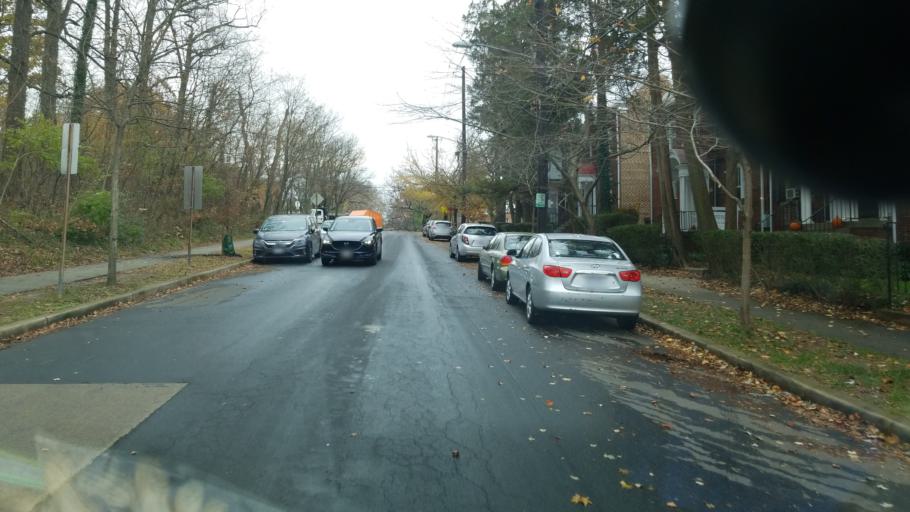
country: US
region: Maryland
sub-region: Montgomery County
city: Friendship Village
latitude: 38.9234
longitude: -77.0805
